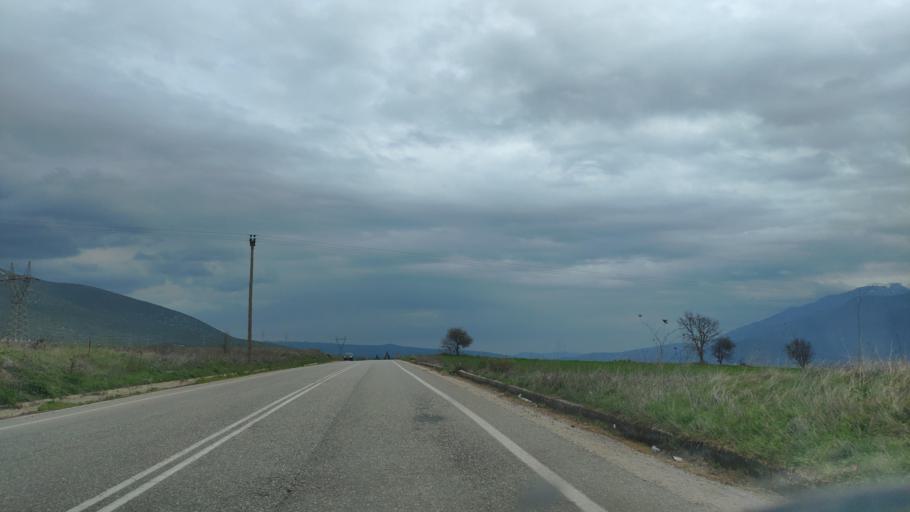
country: GR
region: Central Greece
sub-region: Nomos Fthiotidos
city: Amfikleia
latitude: 38.7105
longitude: 22.4808
